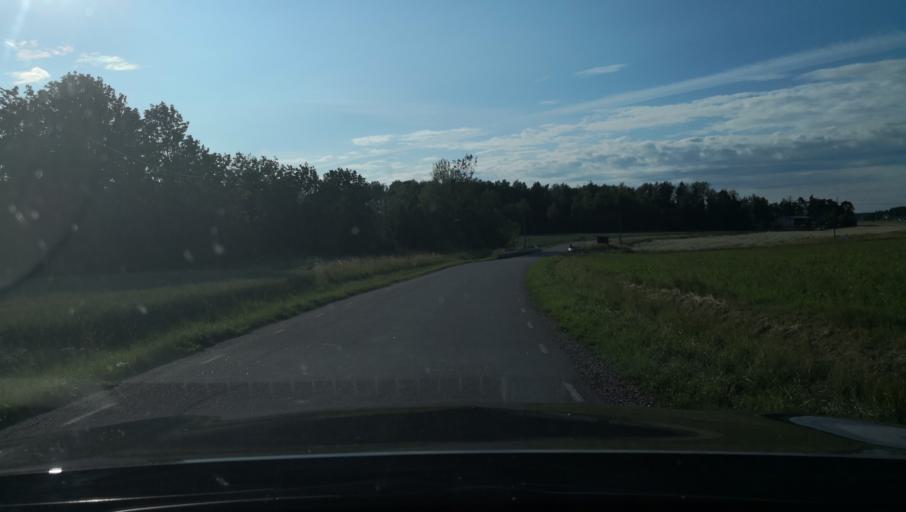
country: SE
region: Uppsala
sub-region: Uppsala Kommun
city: Vattholma
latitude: 59.9321
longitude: 17.8285
